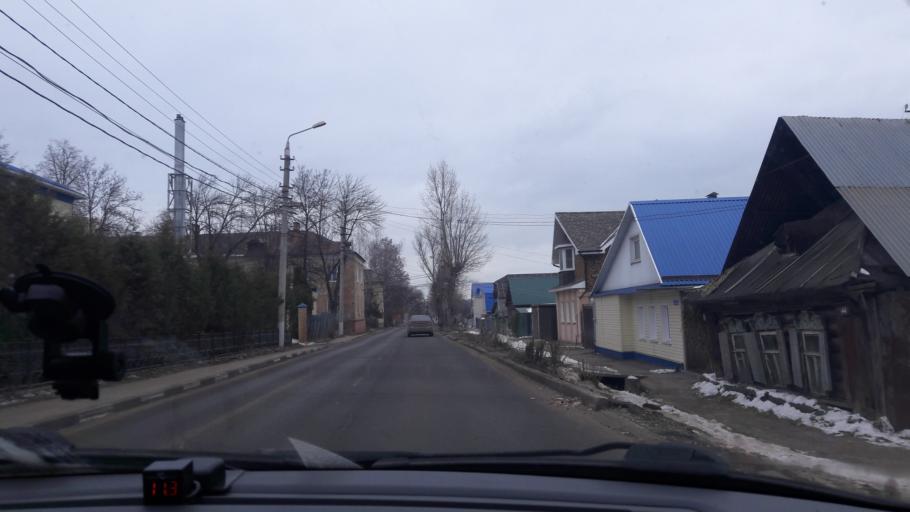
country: RU
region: Tula
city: Tula
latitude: 54.2055
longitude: 37.6556
